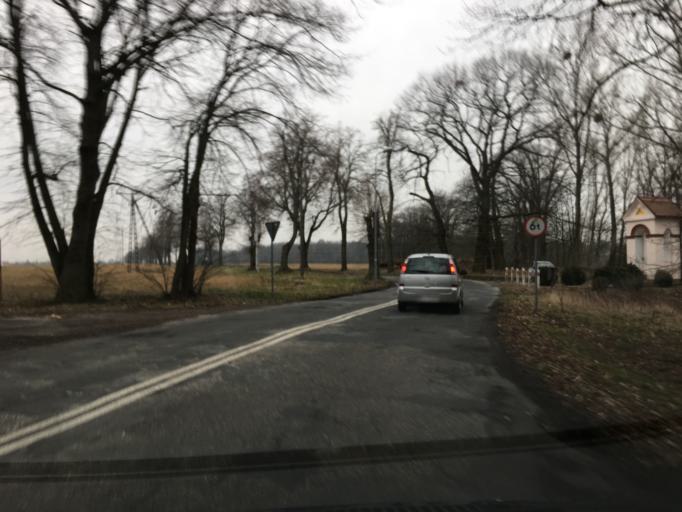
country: PL
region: Opole Voivodeship
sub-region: Powiat kedzierzynsko-kozielski
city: Bierawa
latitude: 50.2969
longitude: 18.2337
